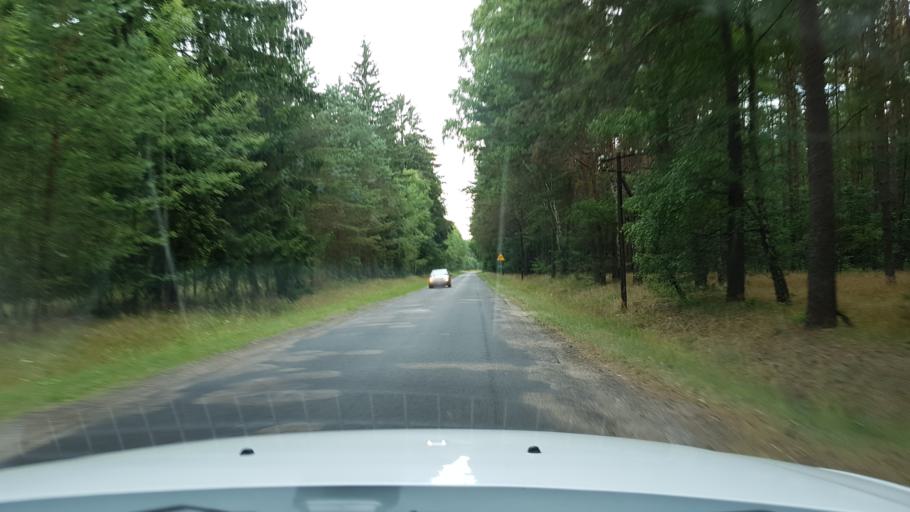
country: PL
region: West Pomeranian Voivodeship
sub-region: Powiat drawski
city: Wierzchowo
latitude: 53.4488
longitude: 16.1355
